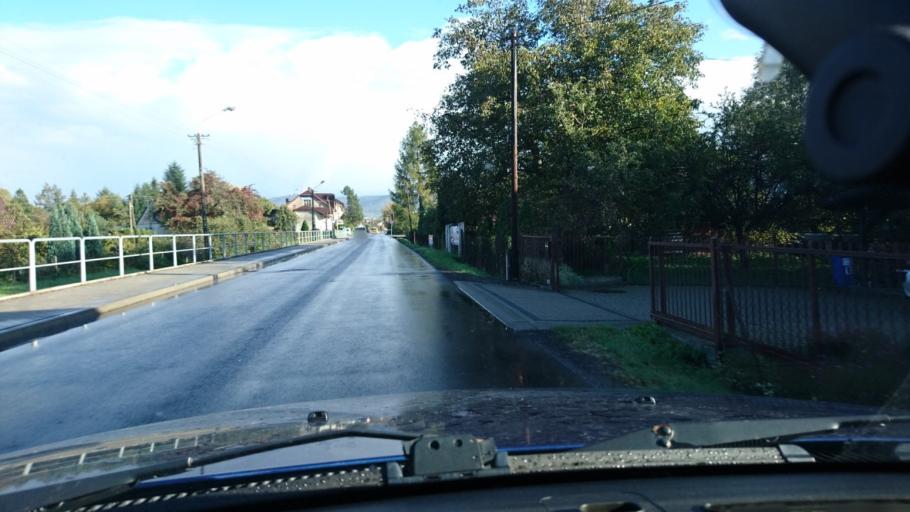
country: PL
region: Silesian Voivodeship
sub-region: Bielsko-Biala
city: Bielsko-Biala
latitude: 49.8501
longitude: 19.0414
